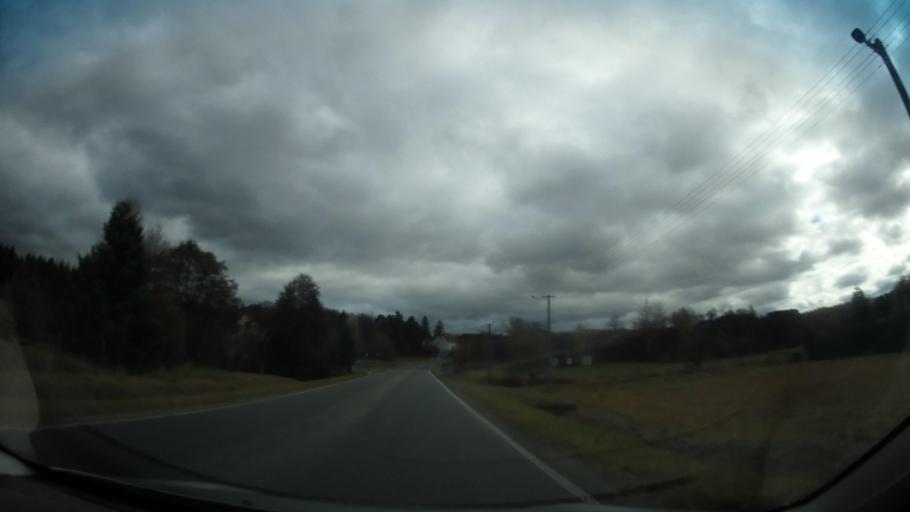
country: CZ
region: Vysocina
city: Budisov
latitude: 49.2850
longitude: 16.1001
